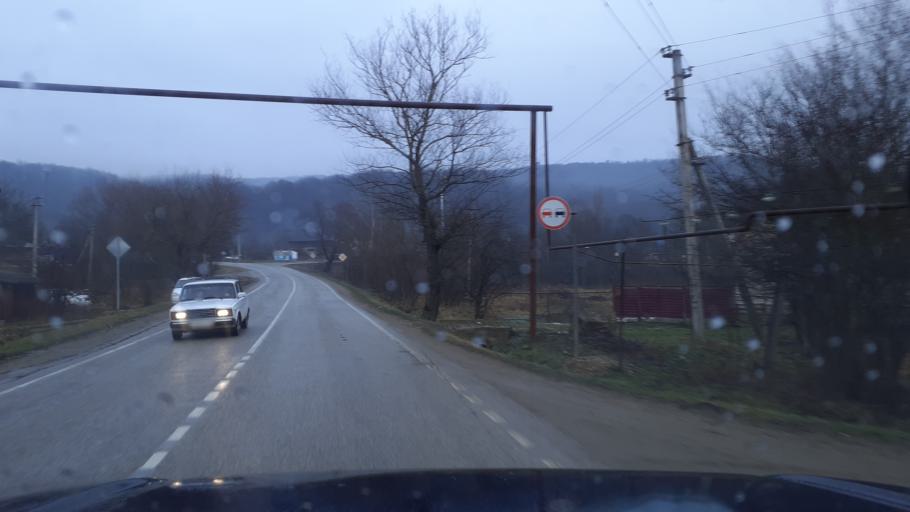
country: RU
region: Krasnodarskiy
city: Neftegorsk
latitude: 44.2980
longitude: 39.8325
